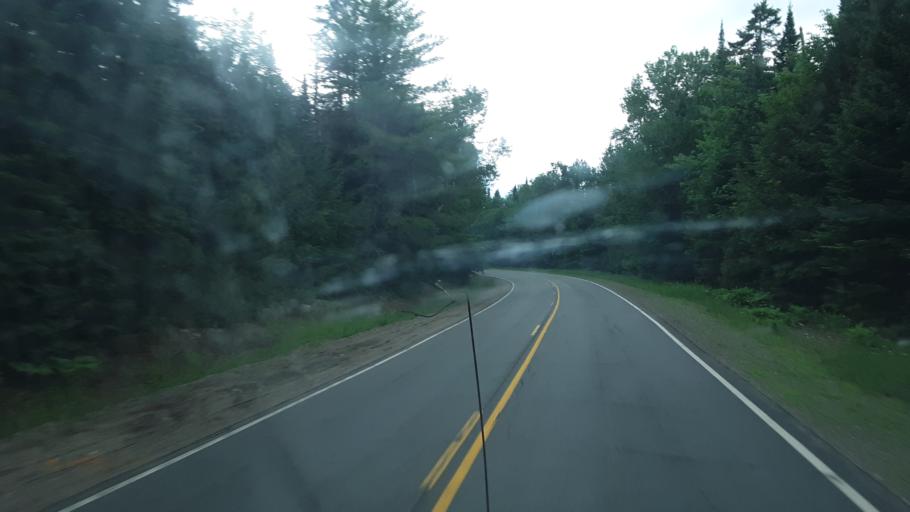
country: US
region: Maine
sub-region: Penobscot County
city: Medway
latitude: 45.7052
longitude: -68.2929
